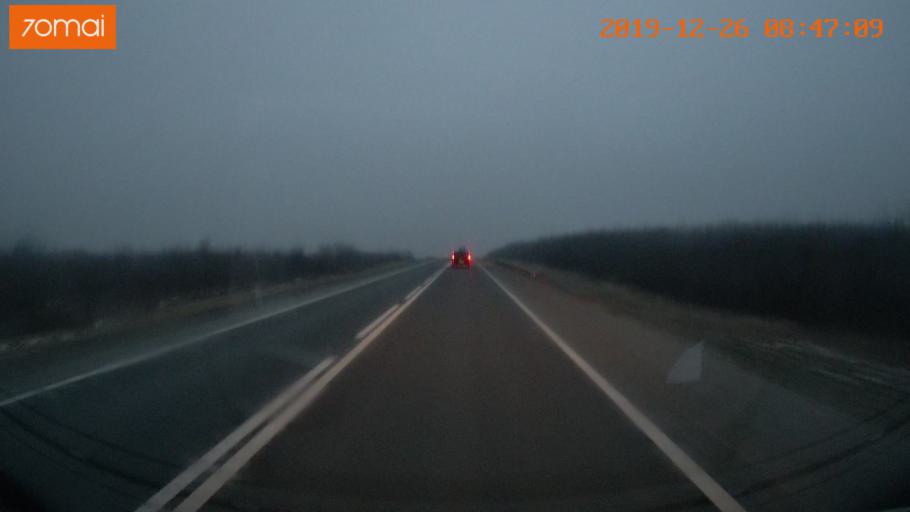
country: RU
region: Jaroslavl
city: Prechistoye
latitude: 58.6196
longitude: 40.3330
